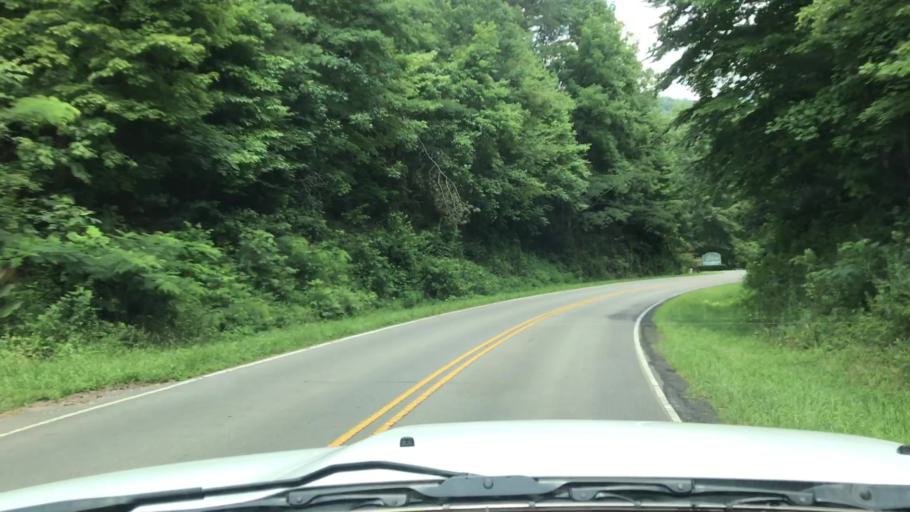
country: US
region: North Carolina
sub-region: Graham County
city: Robbinsville
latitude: 35.3503
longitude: -83.8306
